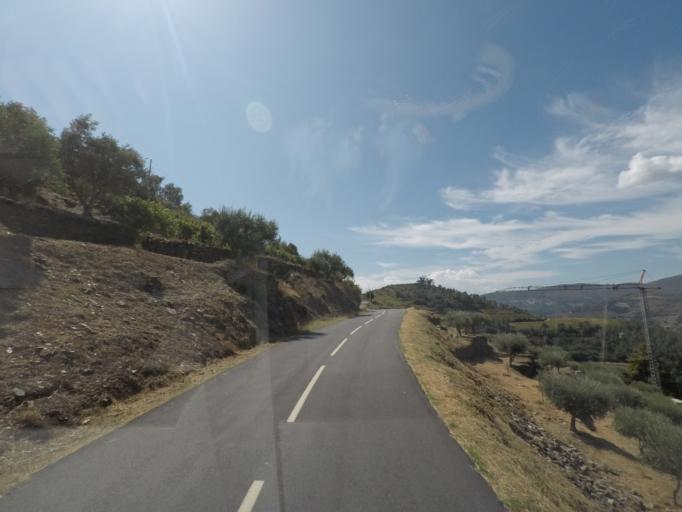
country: PT
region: Vila Real
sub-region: Sabrosa
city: Sabrosa
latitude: 41.2185
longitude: -7.5254
